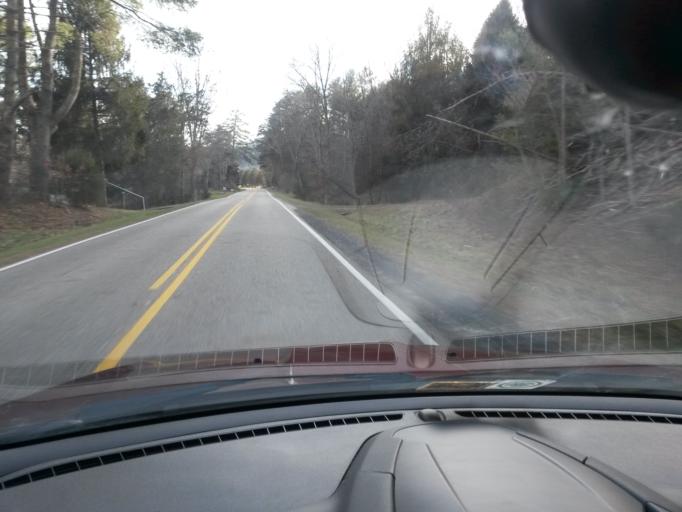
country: US
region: Virginia
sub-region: Alleghany County
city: Clifton Forge
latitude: 37.8873
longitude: -79.7514
